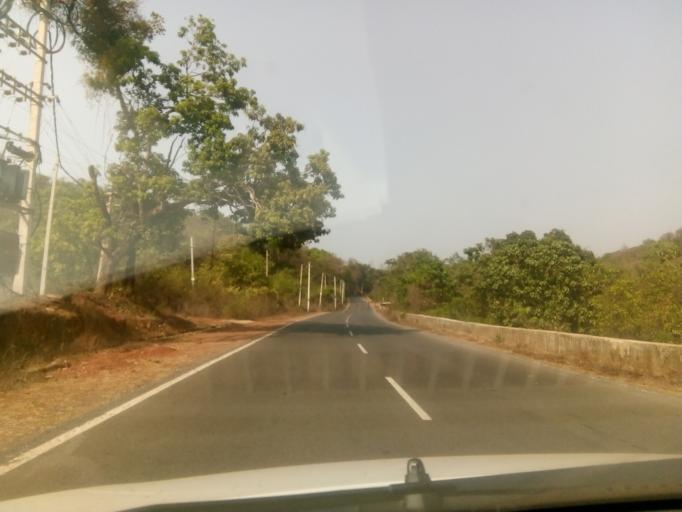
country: IN
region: Goa
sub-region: North Goa
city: Pernem
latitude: 15.7037
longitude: 73.8500
